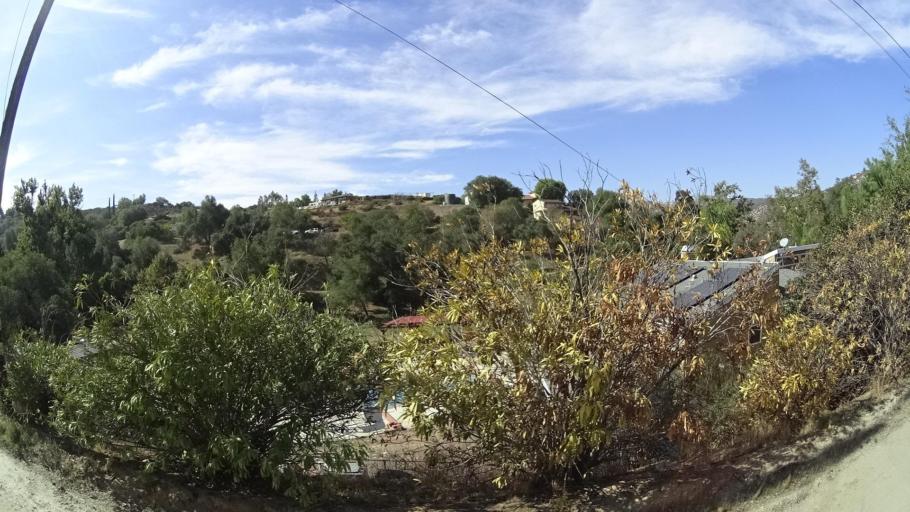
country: US
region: California
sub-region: San Diego County
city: Alpine
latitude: 32.8379
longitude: -116.7995
